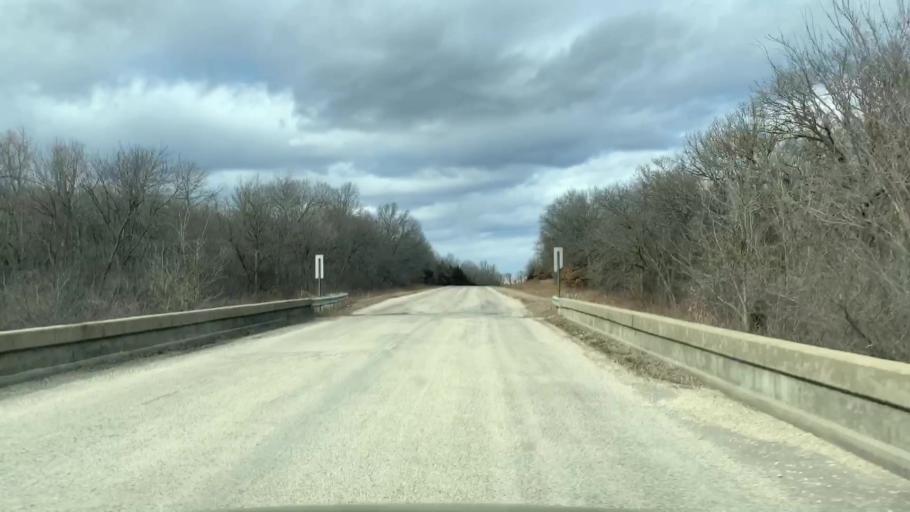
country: US
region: Kansas
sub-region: Allen County
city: Humboldt
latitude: 37.7532
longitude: -95.4712
